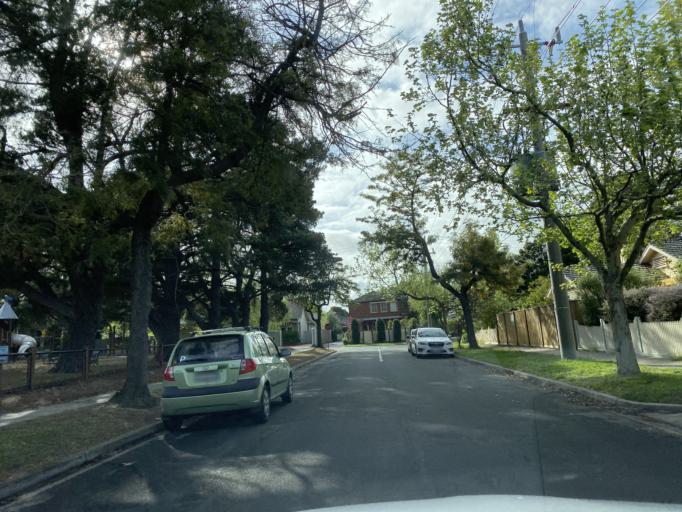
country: AU
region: Victoria
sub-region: Boroondara
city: Canterbury
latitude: -37.8289
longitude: 145.0888
